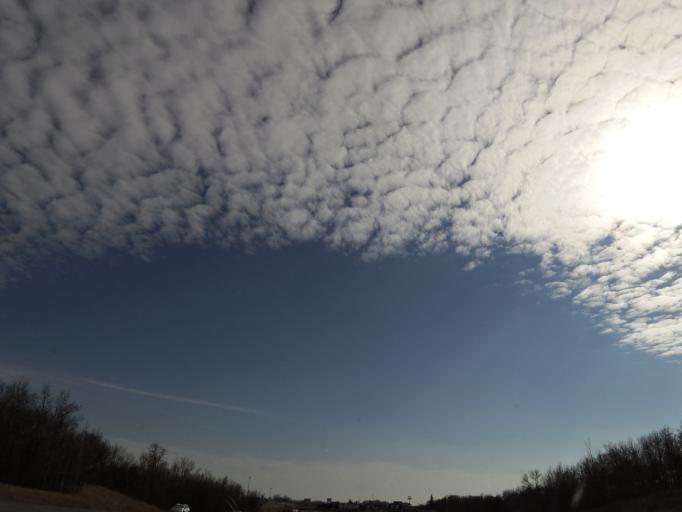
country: US
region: Minnesota
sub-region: Steele County
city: Medford
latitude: 44.1794
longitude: -93.2579
